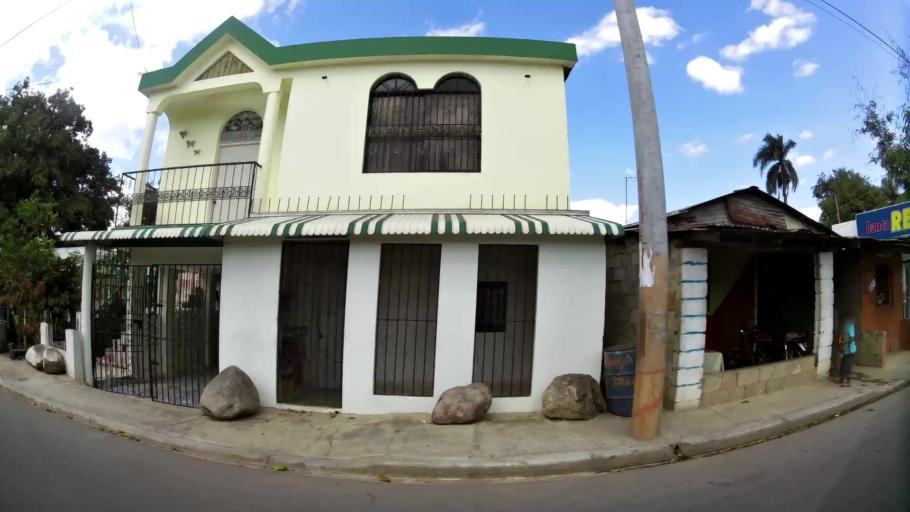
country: DO
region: Santiago
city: Licey al Medio
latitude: 19.3887
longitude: -70.6353
